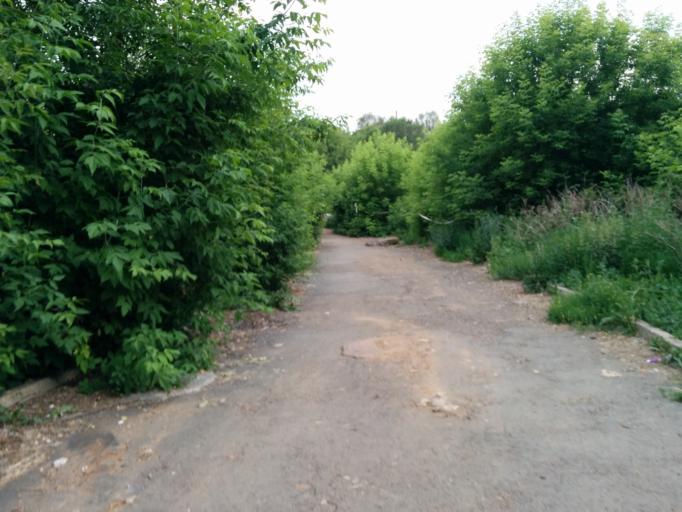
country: RU
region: Perm
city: Perm
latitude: 58.0196
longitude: 56.2646
